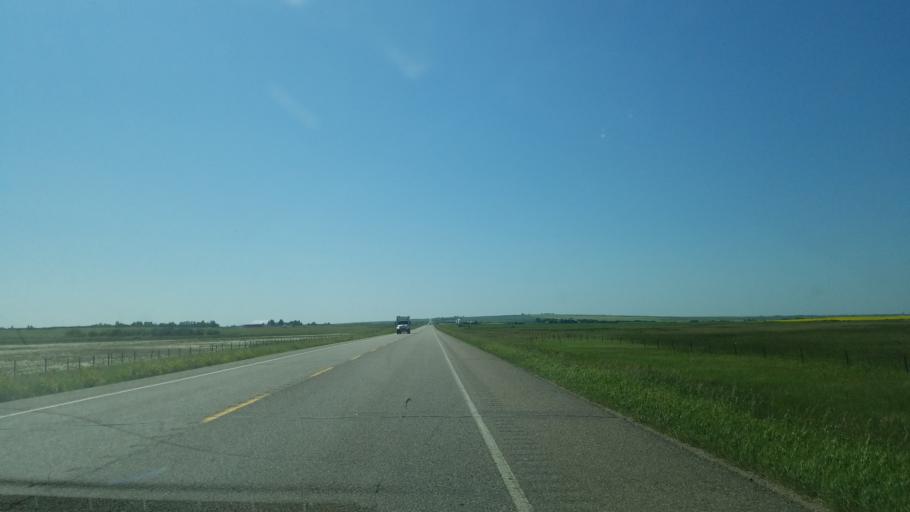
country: CA
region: Saskatchewan
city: Macklin
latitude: 52.3613
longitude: -110.0780
